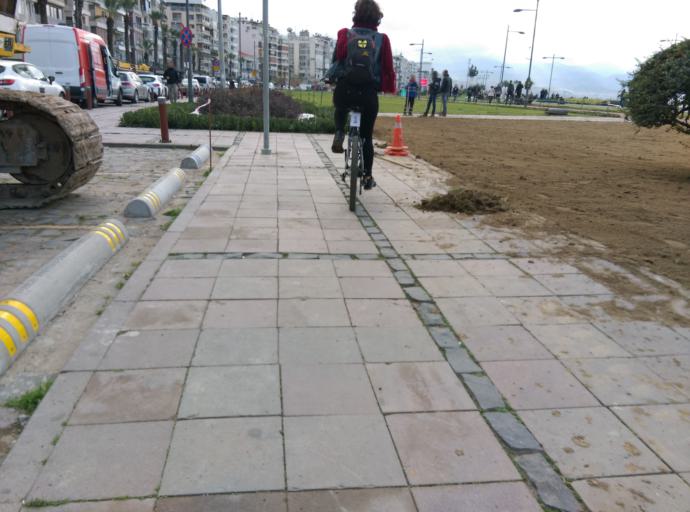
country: TR
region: Izmir
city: Izmir
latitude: 38.4378
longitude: 27.1413
